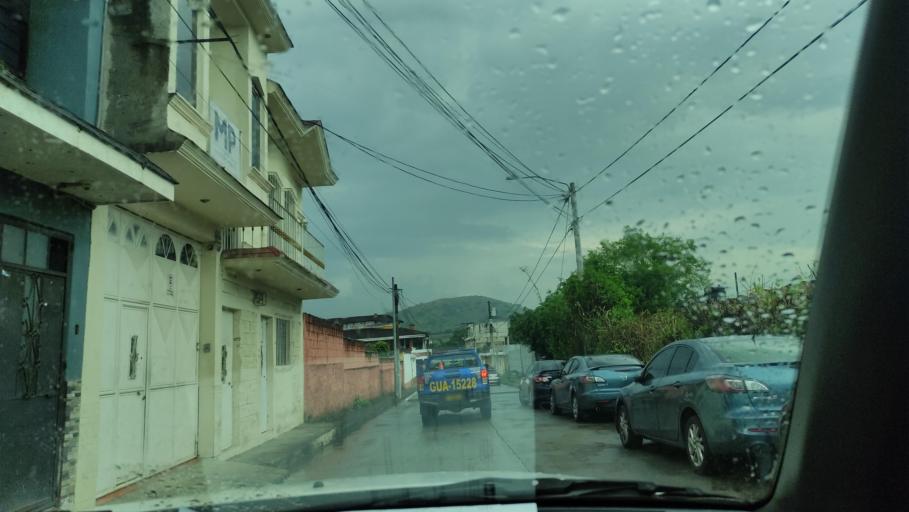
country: GT
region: Guatemala
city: Petapa
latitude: 14.5009
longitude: -90.5580
